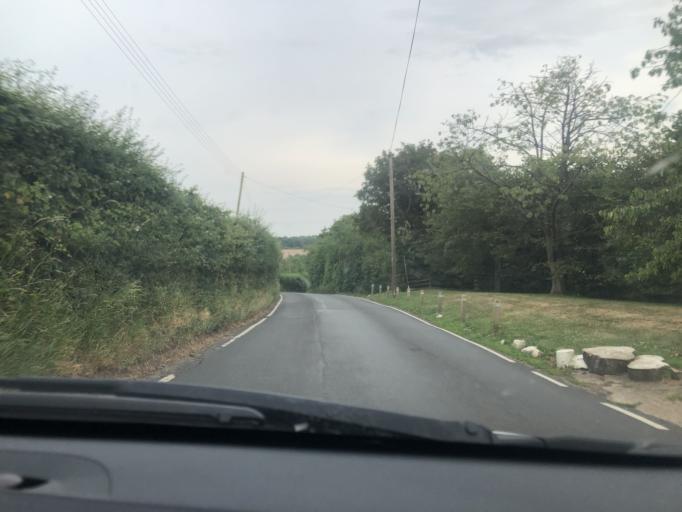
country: GB
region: England
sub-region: Kent
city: Sturry
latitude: 51.3215
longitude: 1.1431
